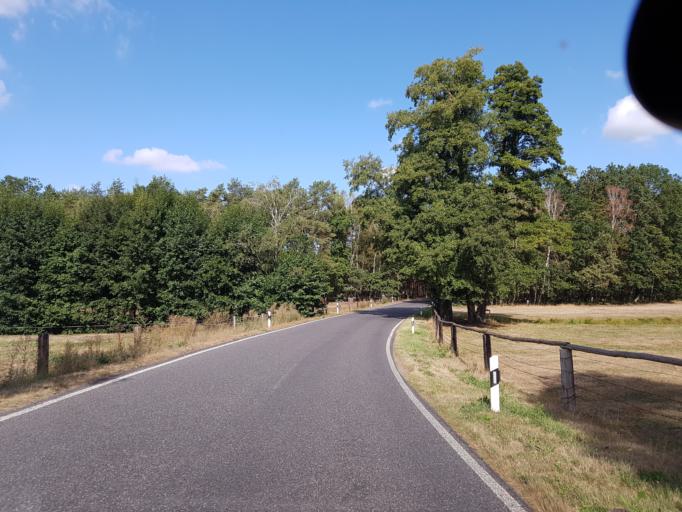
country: DE
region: Brandenburg
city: Sonnewalde
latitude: 51.7409
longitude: 13.6195
